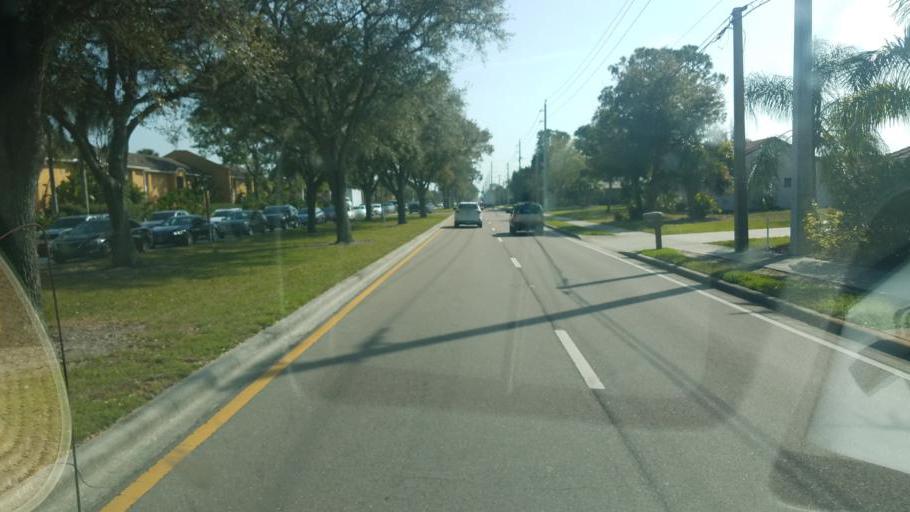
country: US
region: Florida
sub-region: Sarasota County
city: Southgate
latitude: 27.3182
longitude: -82.4976
